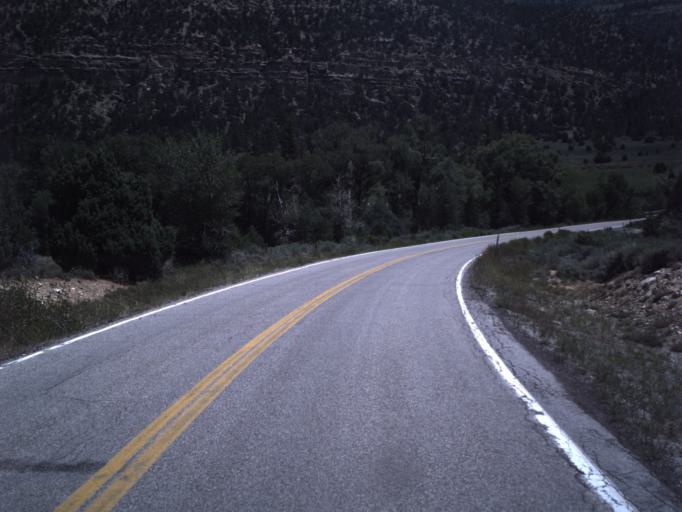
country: US
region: Utah
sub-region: Emery County
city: Orangeville
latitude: 39.3229
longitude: -111.2783
